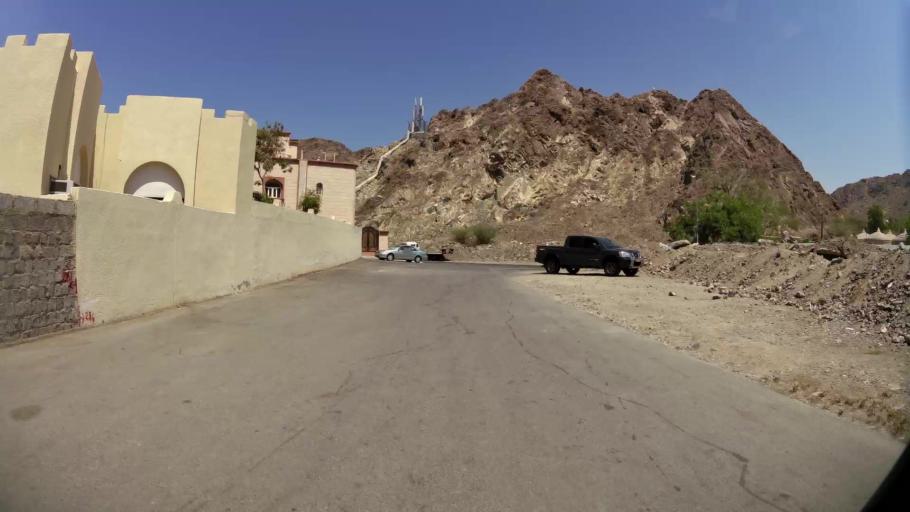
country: OM
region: Muhafazat Masqat
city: Muscat
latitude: 23.5948
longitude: 58.5962
